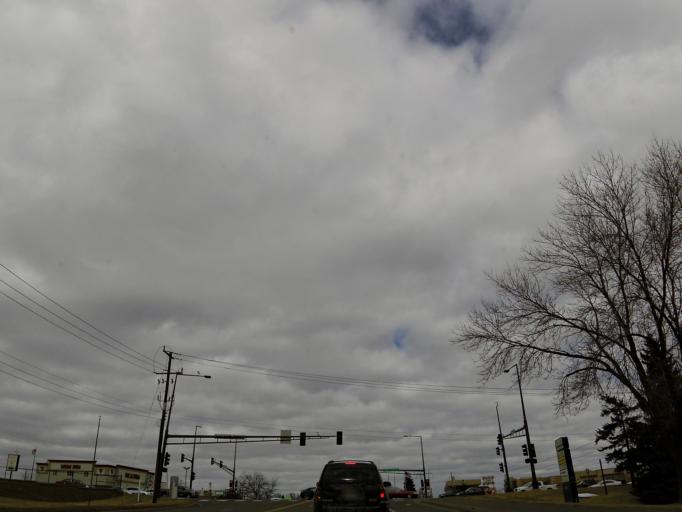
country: US
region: Minnesota
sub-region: Washington County
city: Woodbury
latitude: 44.9247
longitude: -92.9662
